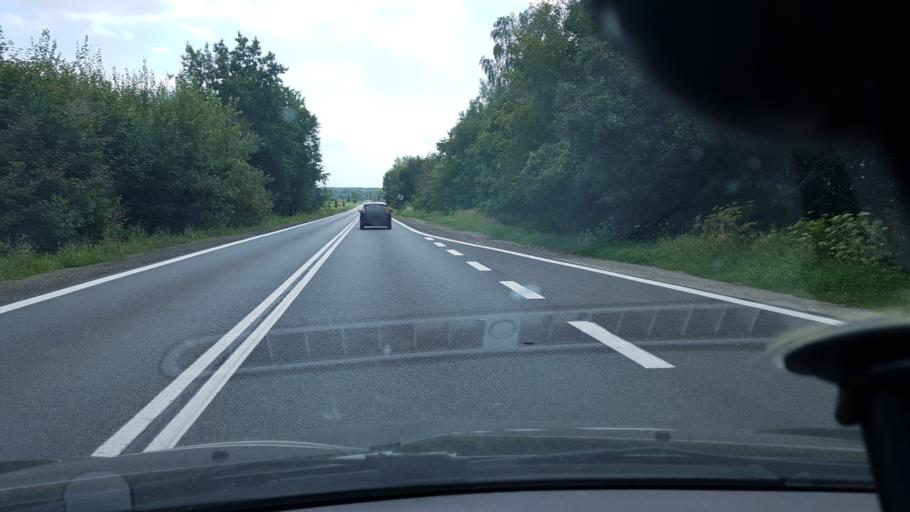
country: PL
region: Silesian Voivodeship
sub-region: Powiat bierunsko-ledzinski
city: Bierun
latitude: 50.0975
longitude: 19.1000
